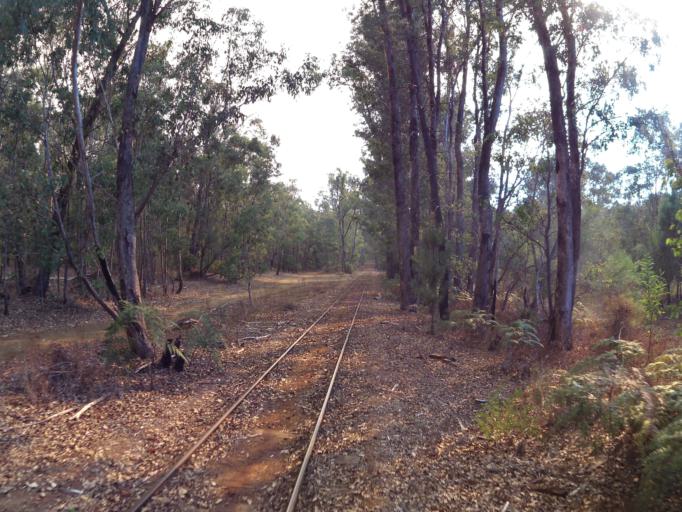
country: AU
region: Western Australia
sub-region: Waroona
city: Waroona
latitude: -32.7387
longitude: 116.1280
